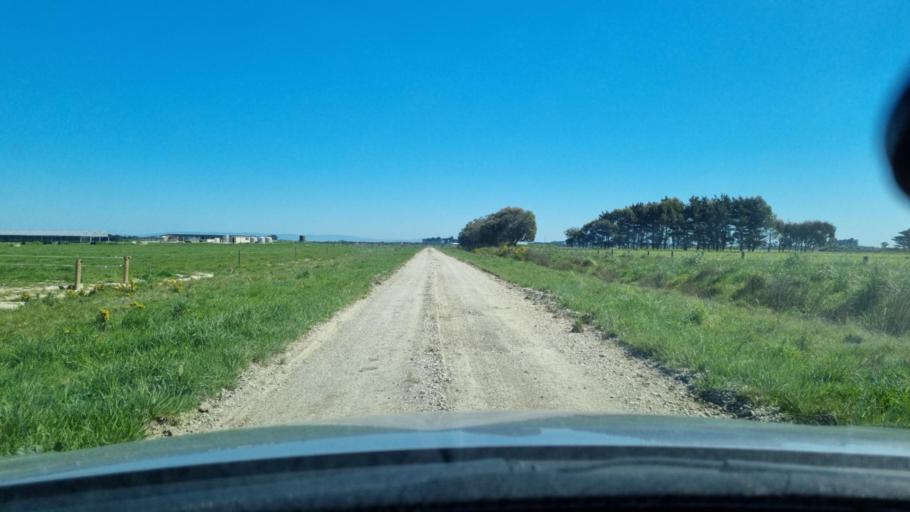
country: NZ
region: Southland
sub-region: Invercargill City
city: Invercargill
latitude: -46.4234
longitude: 168.3141
